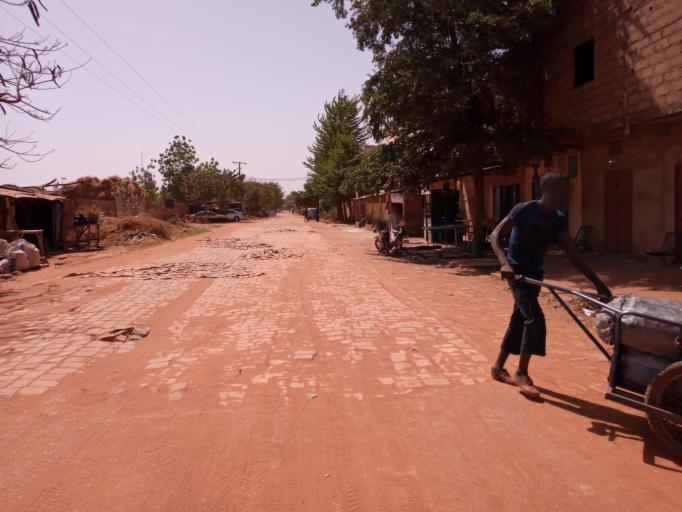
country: ML
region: Bamako
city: Bamako
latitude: 12.5866
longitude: -7.9565
